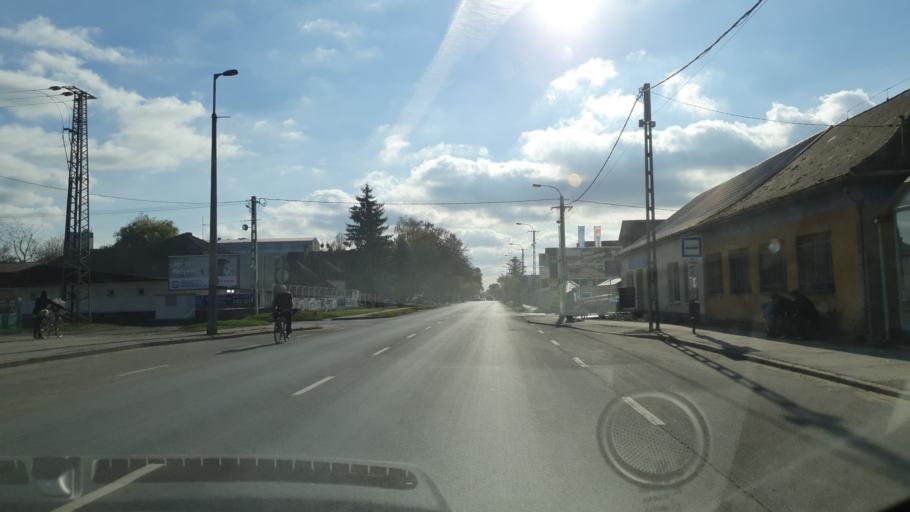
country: HU
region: Szabolcs-Szatmar-Bereg
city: Kisvarda
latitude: 48.2109
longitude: 22.0864
